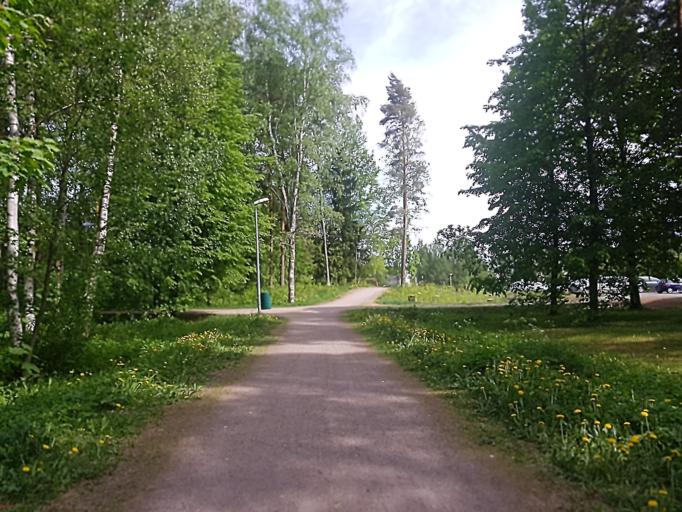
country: FI
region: Uusimaa
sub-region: Helsinki
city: Teekkarikylae
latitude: 60.2739
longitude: 24.8556
